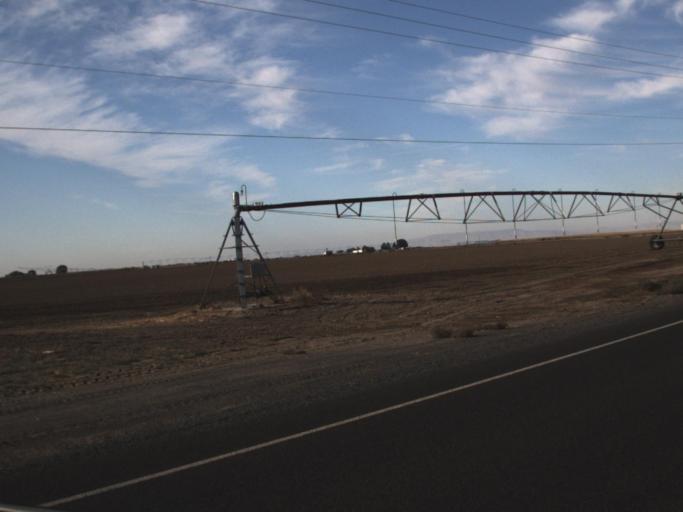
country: US
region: Washington
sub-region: Franklin County
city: Connell
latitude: 46.6637
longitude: -118.9477
